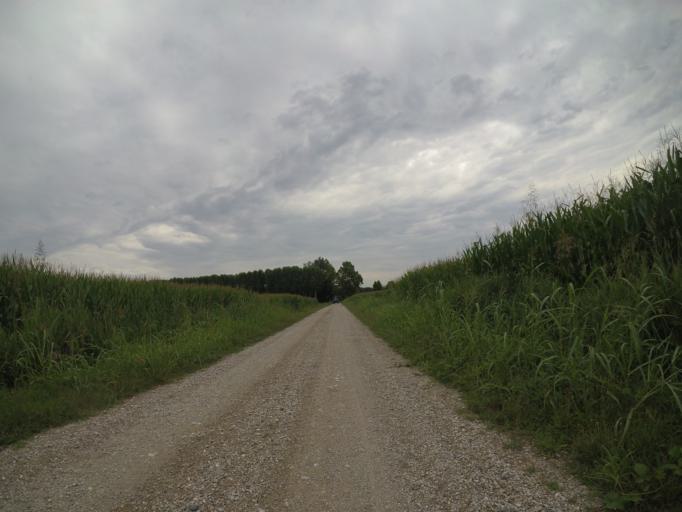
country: IT
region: Friuli Venezia Giulia
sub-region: Provincia di Udine
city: Rivignano
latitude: 45.9062
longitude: 13.0617
